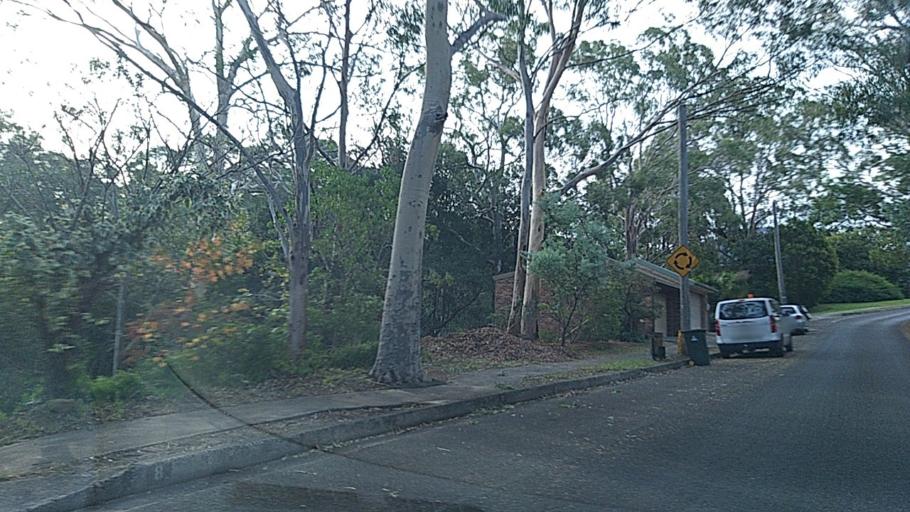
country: AU
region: New South Wales
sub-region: Wollongong
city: Mount Keira
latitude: -34.4287
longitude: 150.8539
